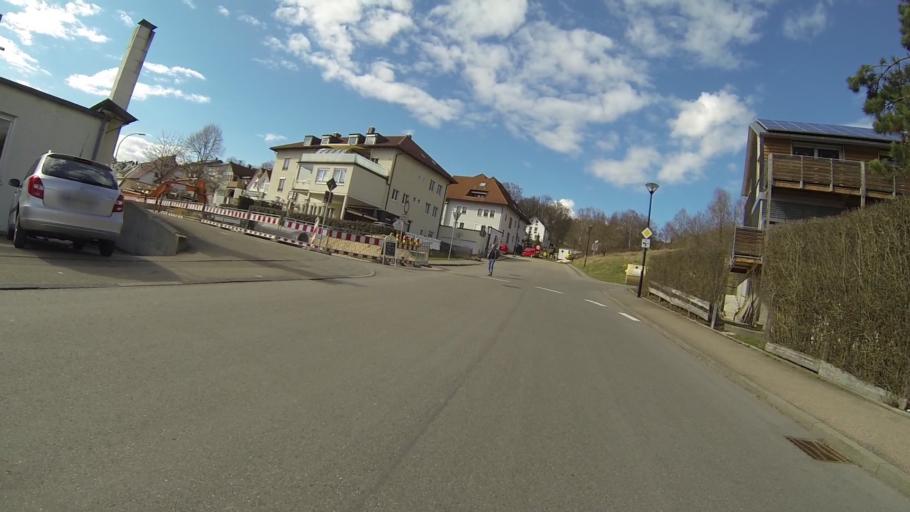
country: DE
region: Baden-Wuerttemberg
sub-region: Regierungsbezirk Stuttgart
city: Heidenheim an der Brenz
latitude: 48.6817
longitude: 10.1301
